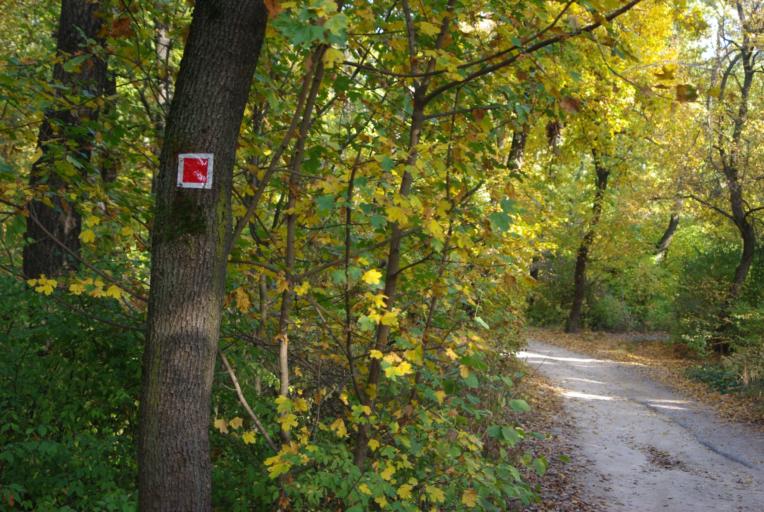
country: HU
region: Pest
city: Budaors
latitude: 47.4792
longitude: 18.9629
